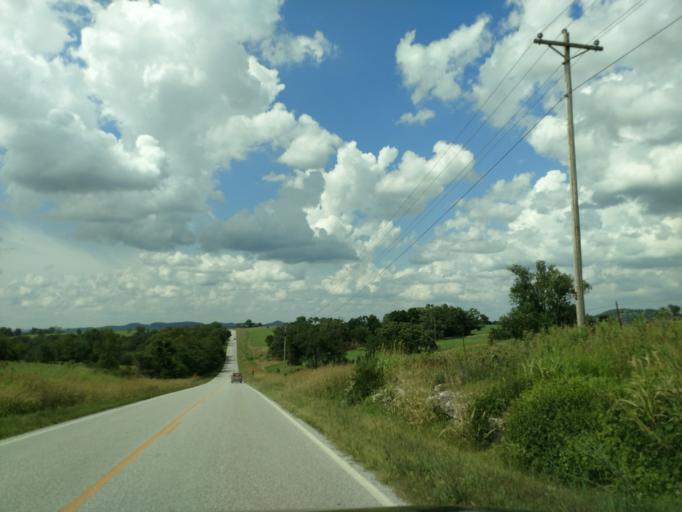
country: US
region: Arkansas
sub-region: Carroll County
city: Berryville
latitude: 36.4605
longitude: -93.5558
